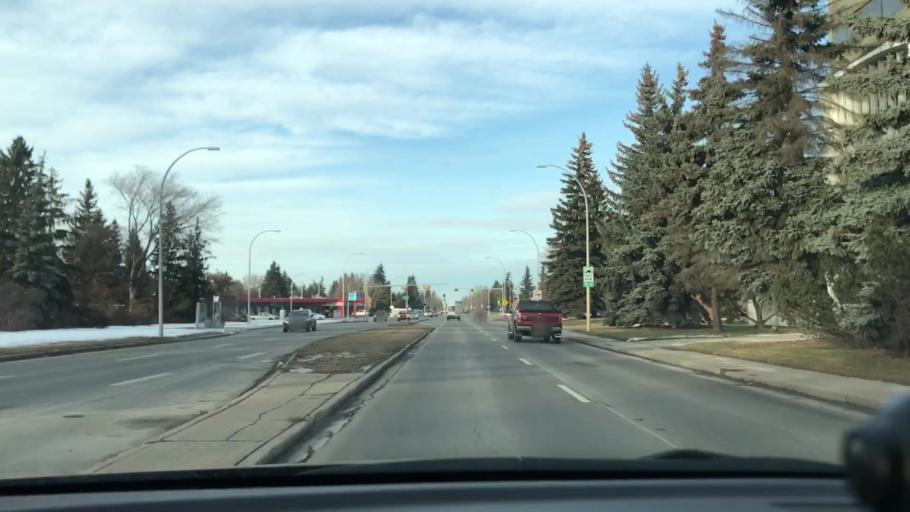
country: CA
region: Alberta
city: Edmonton
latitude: 53.5237
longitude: -113.4429
